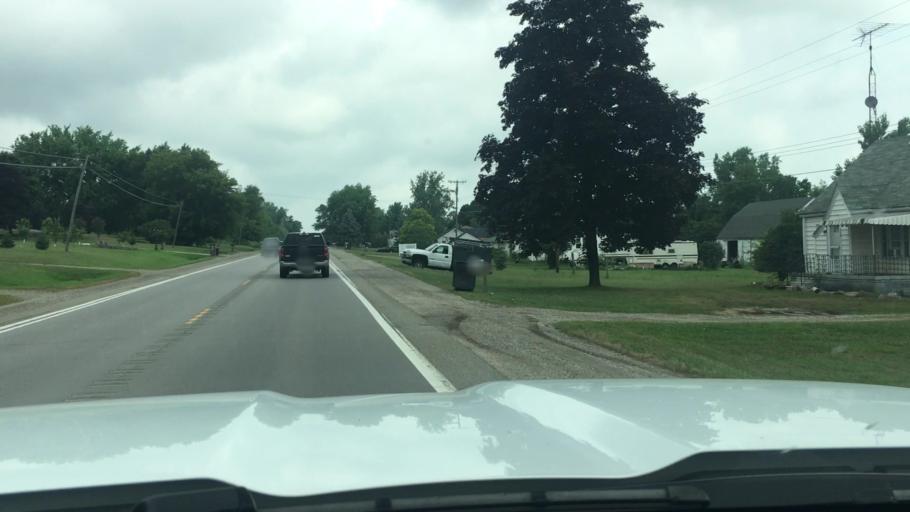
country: US
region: Michigan
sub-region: Lapeer County
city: Imlay City
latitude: 43.0378
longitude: -83.0719
